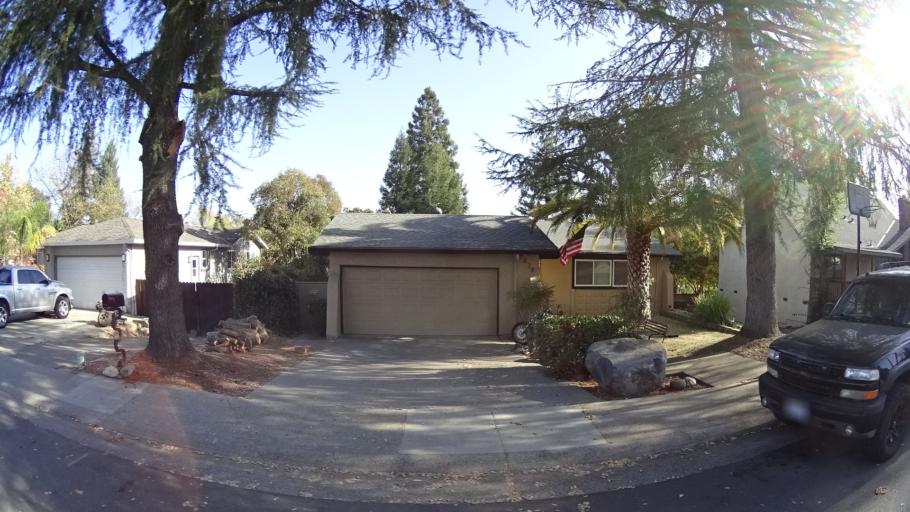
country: US
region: California
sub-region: Sacramento County
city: Orangevale
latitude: 38.6966
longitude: -121.2469
